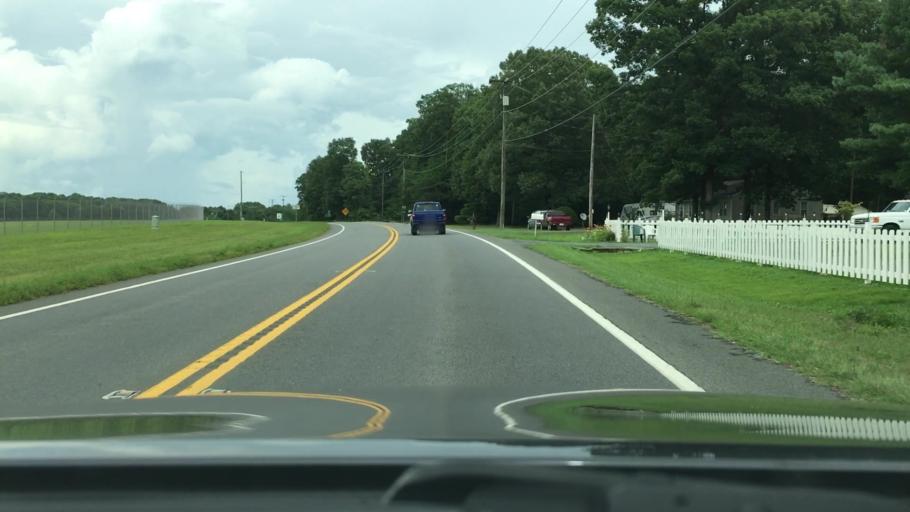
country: US
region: Virginia
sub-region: Orange County
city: Orange
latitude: 38.2471
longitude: -78.0405
